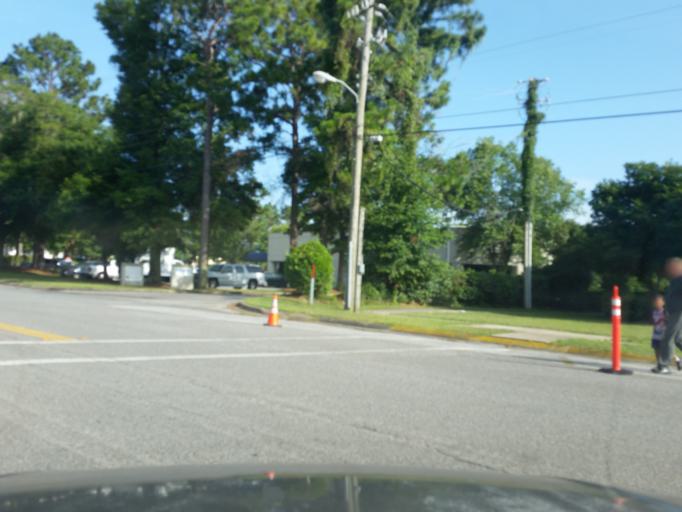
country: US
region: Florida
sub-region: Escambia County
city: Ferry Pass
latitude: 30.4786
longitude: -87.2000
